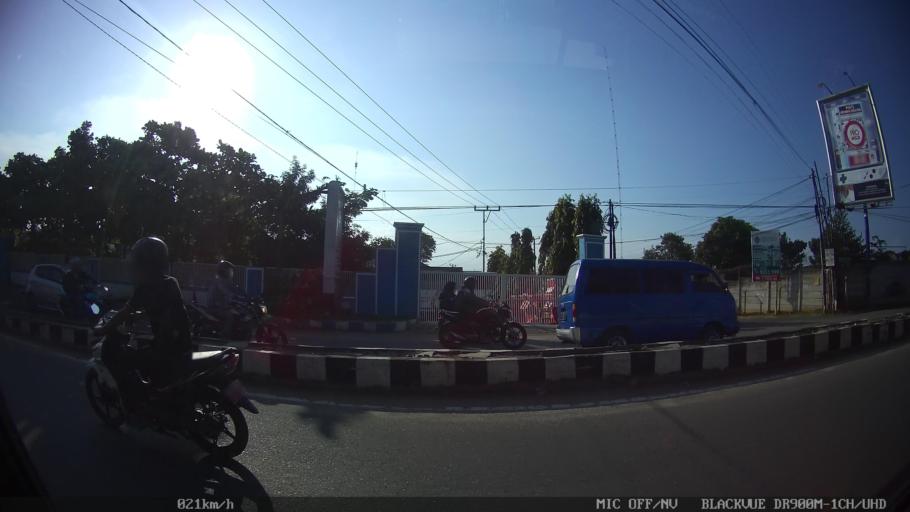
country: ID
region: Lampung
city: Kedaton
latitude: -5.3738
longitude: 105.2230
